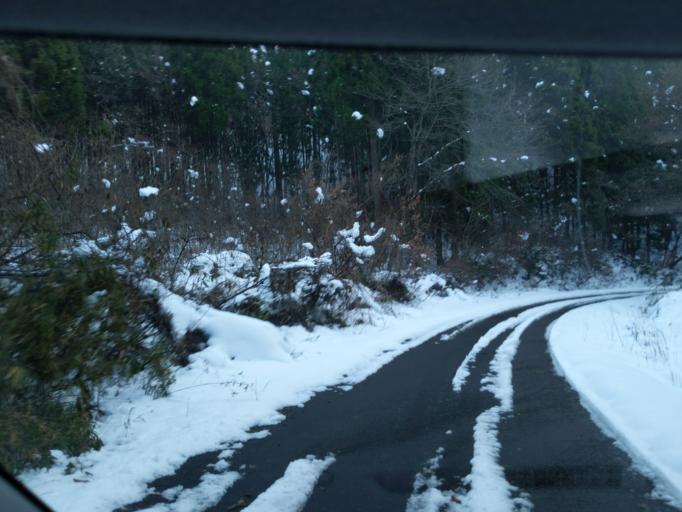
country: JP
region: Iwate
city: Mizusawa
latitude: 39.0517
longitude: 141.0577
